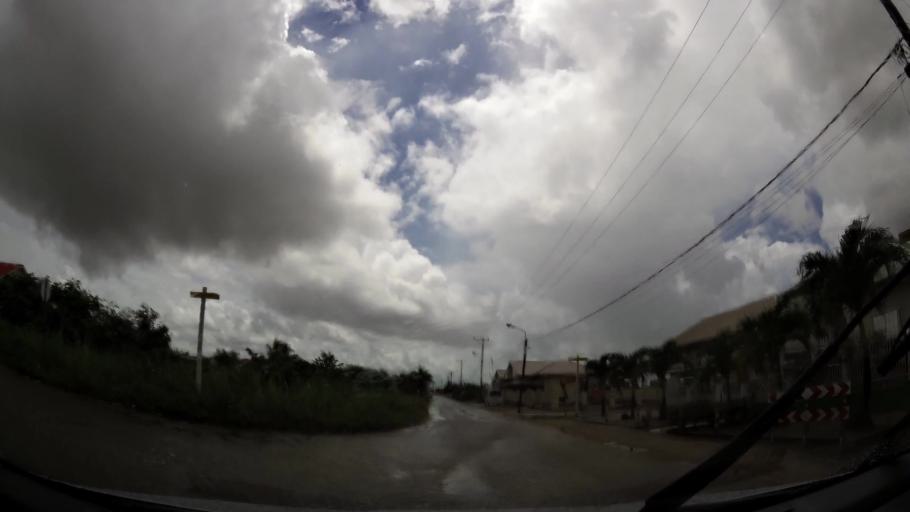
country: SR
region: Paramaribo
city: Paramaribo
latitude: 5.8290
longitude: -55.2332
